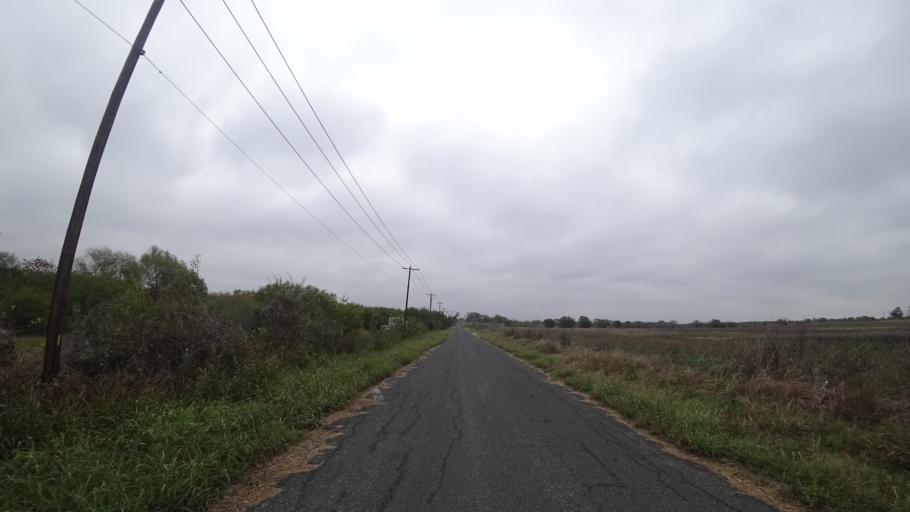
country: US
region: Texas
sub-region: Travis County
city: Pflugerville
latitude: 30.4188
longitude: -97.6186
